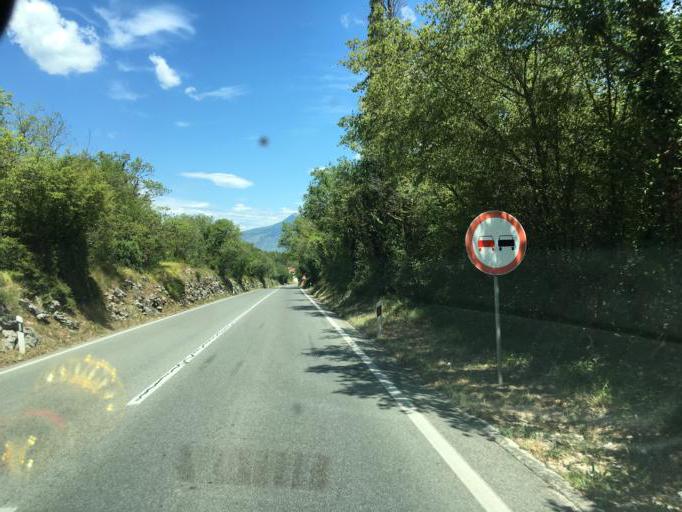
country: HR
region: Istarska
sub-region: Grad Labin
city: Labin
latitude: 45.1428
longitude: 14.1484
